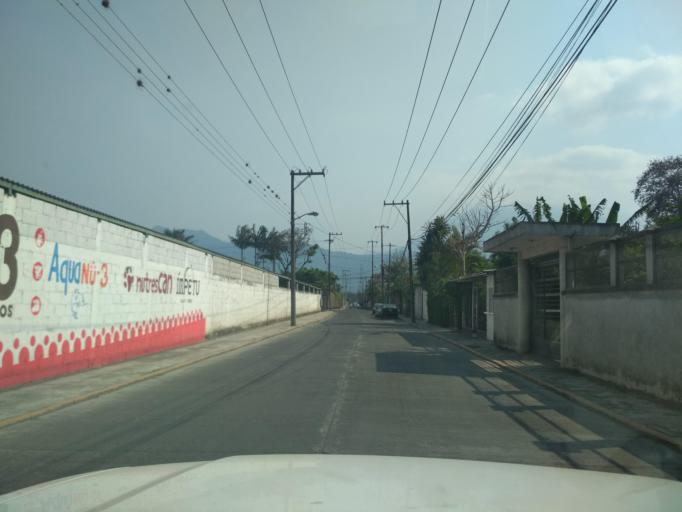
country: MX
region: Veracruz
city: Jalapilla
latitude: 18.8394
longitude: -97.0856
